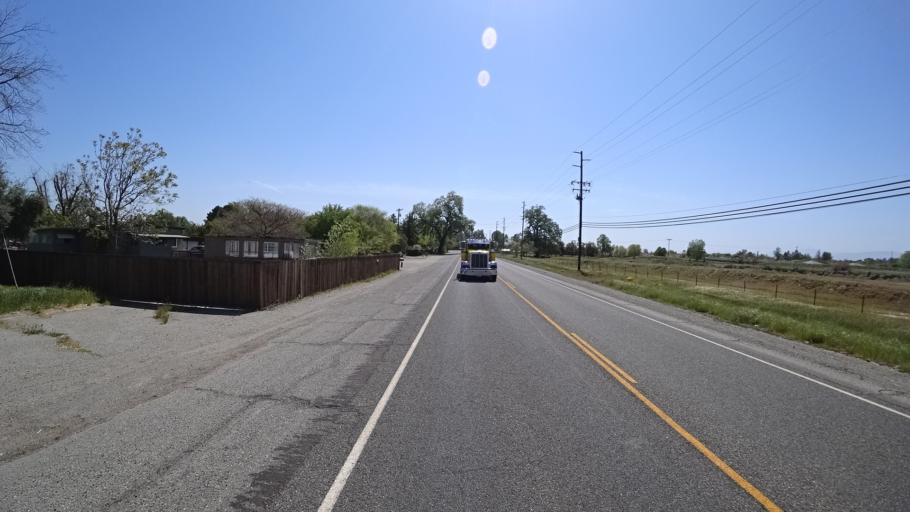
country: US
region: California
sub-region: Glenn County
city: Orland
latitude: 39.7638
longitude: -122.1968
